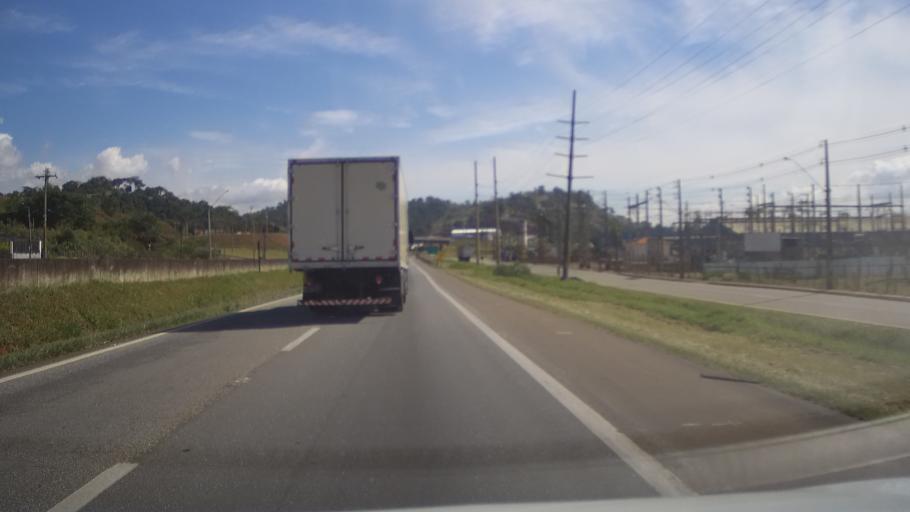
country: BR
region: Minas Gerais
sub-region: Cambui
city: Cambui
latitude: -22.5978
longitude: -46.0569
